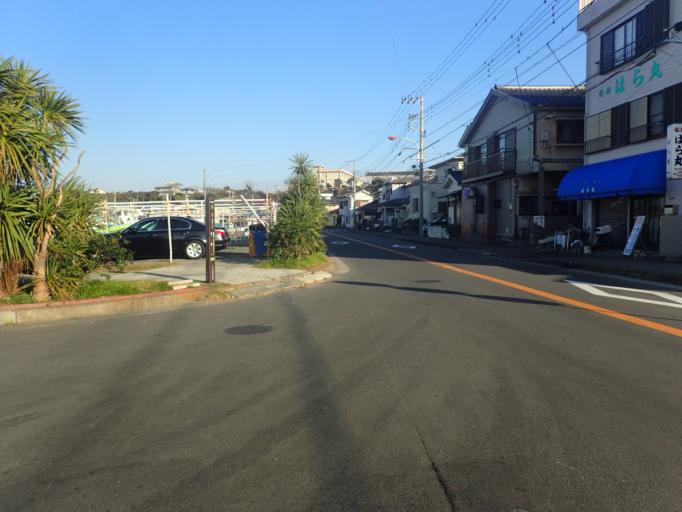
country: JP
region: Kanagawa
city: Miura
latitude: 35.2053
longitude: 139.6092
